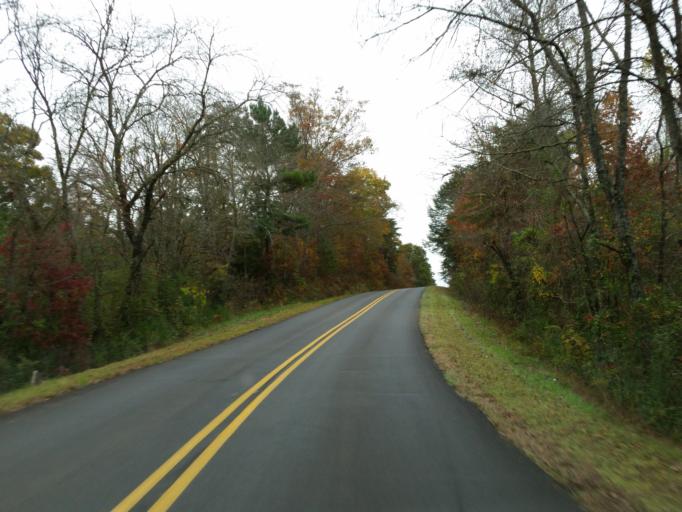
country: US
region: Georgia
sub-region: Gilmer County
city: Ellijay
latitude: 34.6495
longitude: -84.3070
